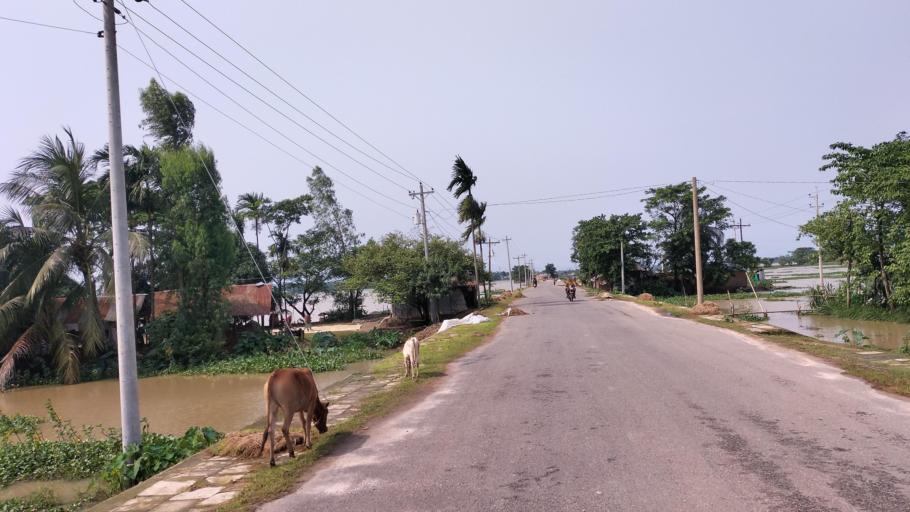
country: BD
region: Dhaka
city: Netrakona
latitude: 25.0167
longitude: 90.8558
